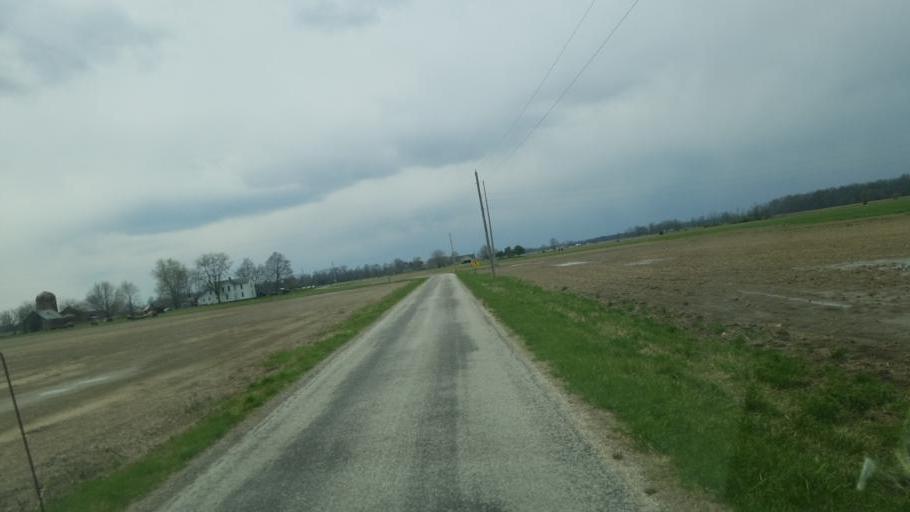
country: US
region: Ohio
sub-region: Marion County
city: Prospect
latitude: 40.3865
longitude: -83.2207
